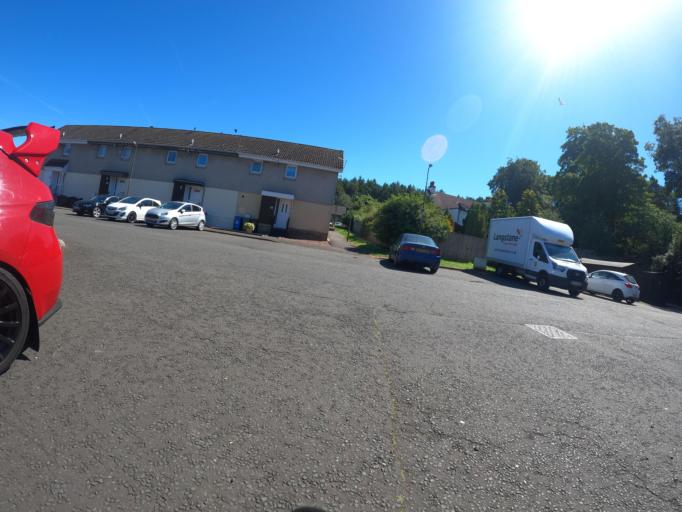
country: GB
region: Scotland
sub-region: West Lothian
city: Livingston
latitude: 55.9205
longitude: -3.5430
